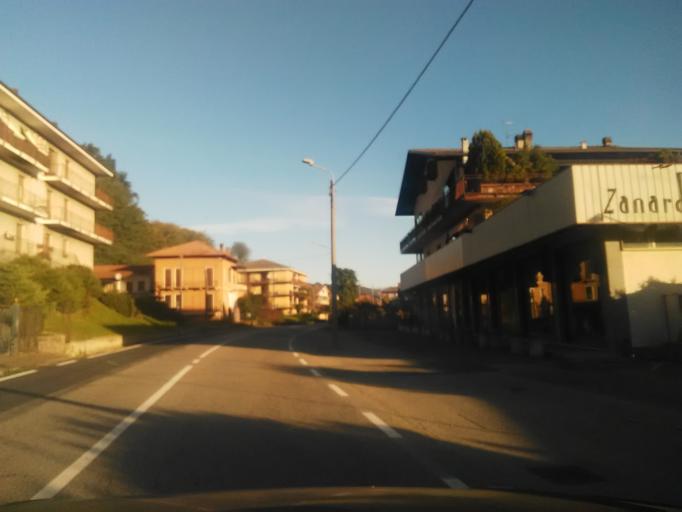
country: IT
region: Piedmont
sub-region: Provincia di Vercelli
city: San Maurizio
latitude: 45.6032
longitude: 8.2897
